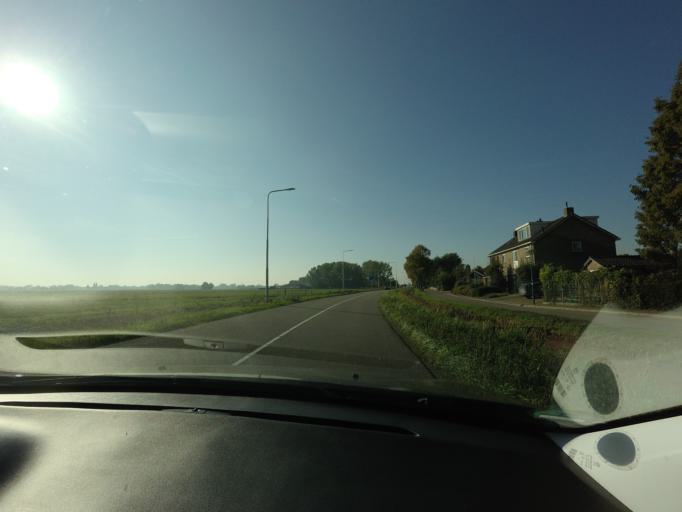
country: NL
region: Utrecht
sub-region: Gemeente Woerden
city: Woerden
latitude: 52.1101
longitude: 4.8973
